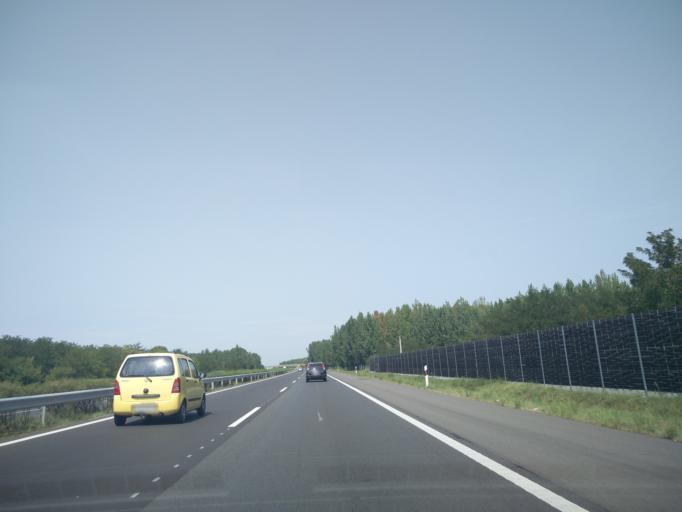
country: HU
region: Bacs-Kiskun
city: Kiskunfelegyhaza
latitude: 46.6533
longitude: 19.8330
